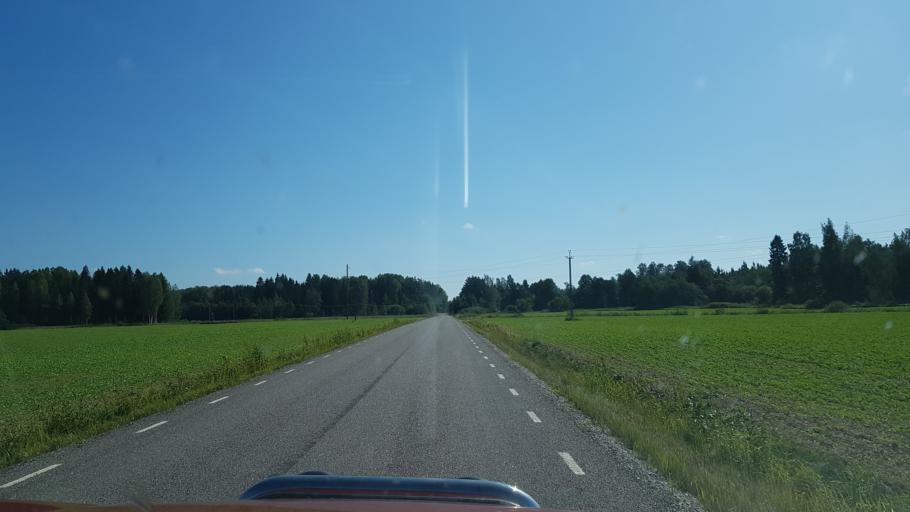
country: EE
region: Polvamaa
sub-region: Polva linn
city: Polva
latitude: 58.2153
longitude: 27.2188
